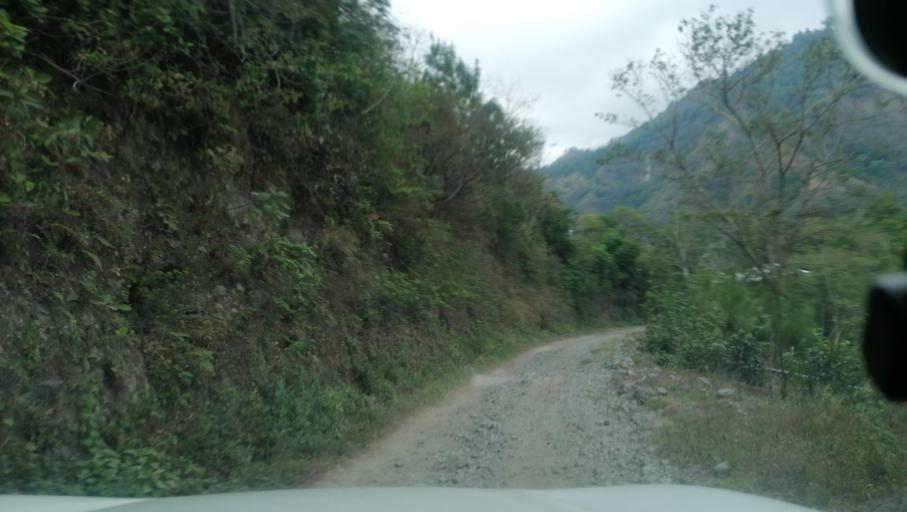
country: GT
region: San Marcos
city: Sibinal
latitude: 15.1668
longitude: -92.1622
